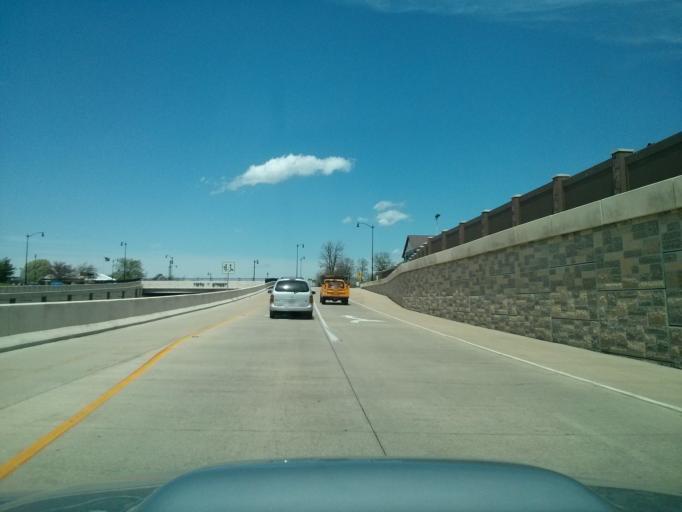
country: US
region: Indiana
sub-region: Hamilton County
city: Carmel
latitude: 39.9551
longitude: -86.1137
